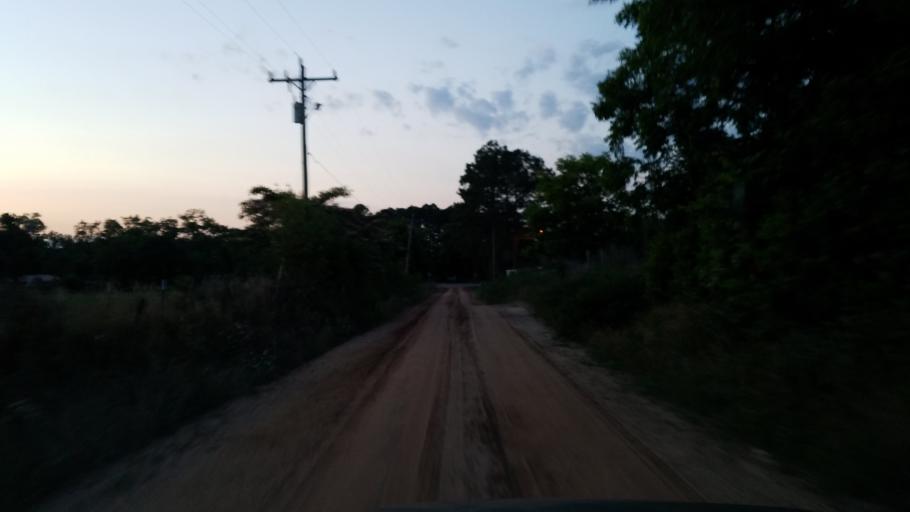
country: US
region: Georgia
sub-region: Turner County
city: Ashburn
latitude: 31.6649
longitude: -83.6266
